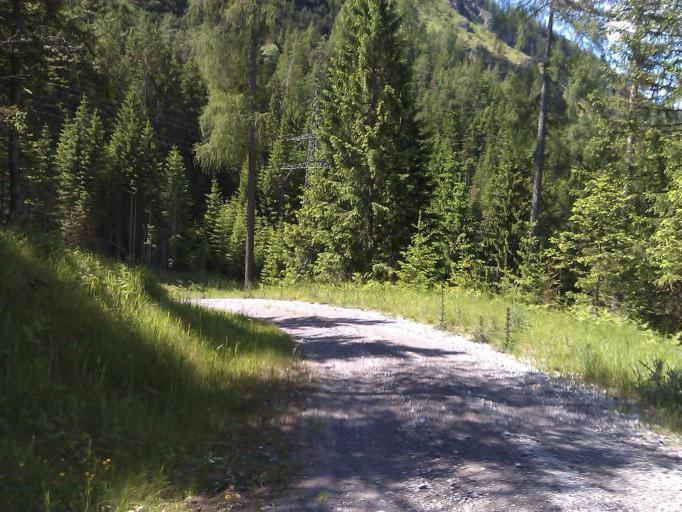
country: AT
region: Tyrol
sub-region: Politischer Bezirk Imst
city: Nassereith
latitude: 47.3561
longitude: 10.8557
